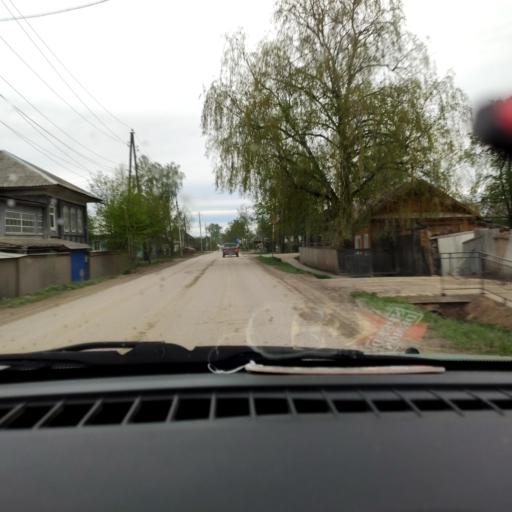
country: RU
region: Perm
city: Kudymkar
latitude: 59.0074
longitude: 54.6572
